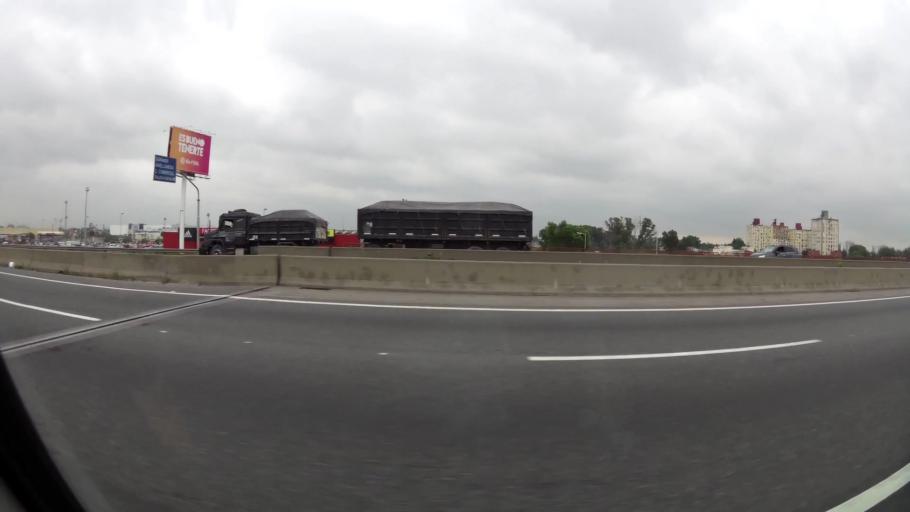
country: AR
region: Buenos Aires
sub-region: Partido de Avellaneda
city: Avellaneda
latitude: -34.6746
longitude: -58.3327
